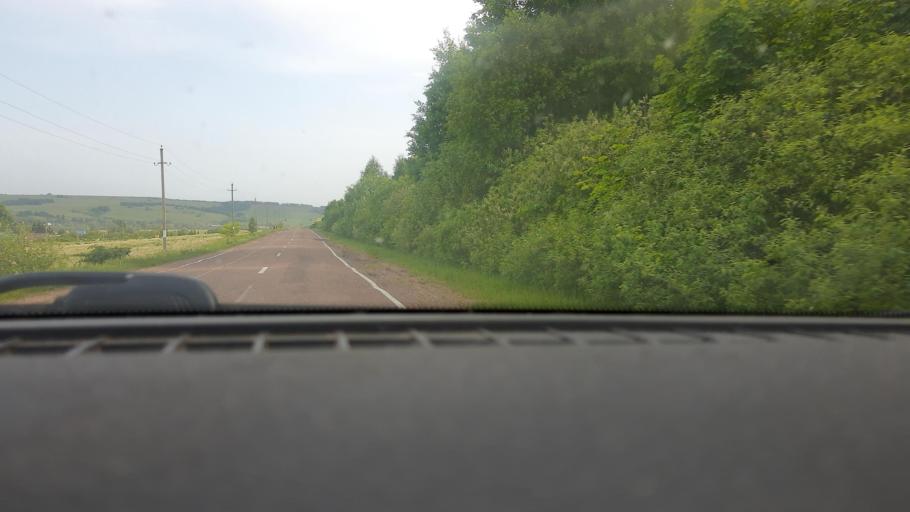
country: RU
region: Bashkortostan
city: Ulukulevo
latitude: 54.5597
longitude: 56.4345
